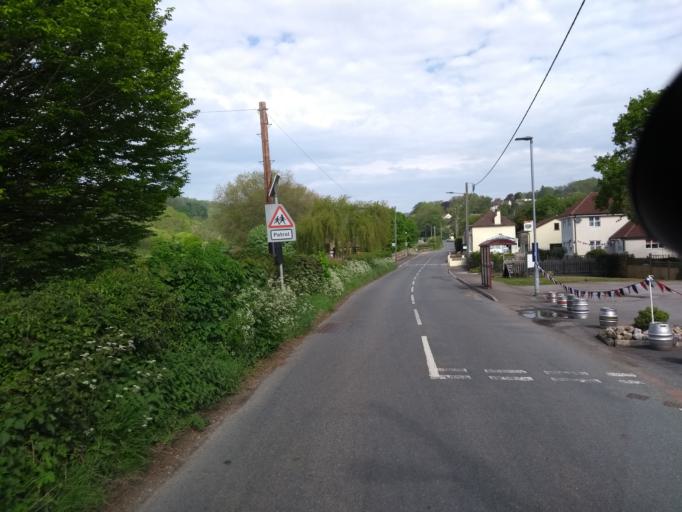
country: GB
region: England
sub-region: Dorset
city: Lyme Regis
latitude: 50.7354
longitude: -2.9582
